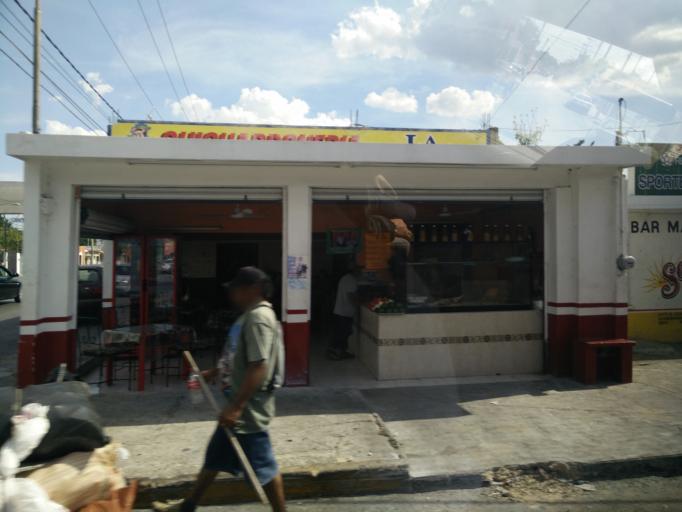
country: MX
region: Yucatan
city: Merida
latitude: 20.9644
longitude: -89.5916
